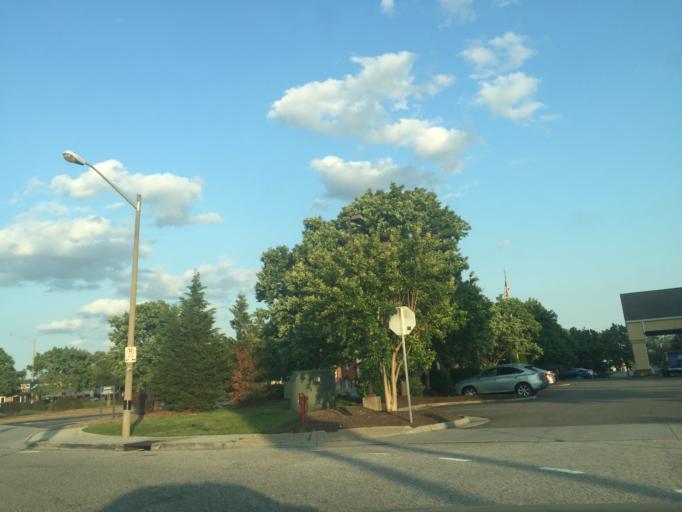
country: US
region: Virginia
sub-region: York County
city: Yorktown
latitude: 37.1122
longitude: -76.5005
